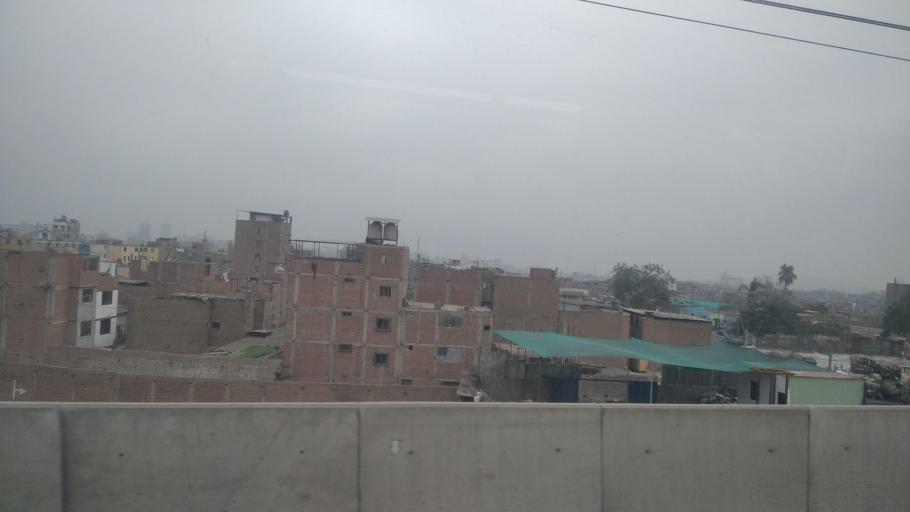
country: PE
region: Lima
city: Lima
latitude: -12.0444
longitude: -77.0103
